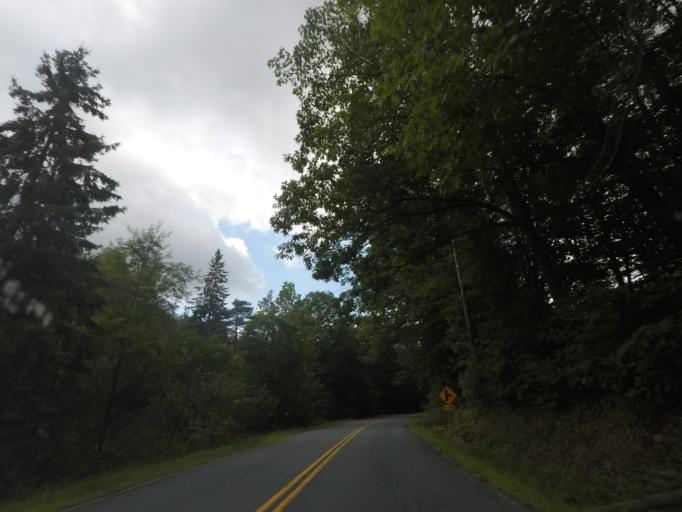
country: US
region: New York
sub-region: Rensselaer County
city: Averill Park
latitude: 42.6454
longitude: -73.5154
